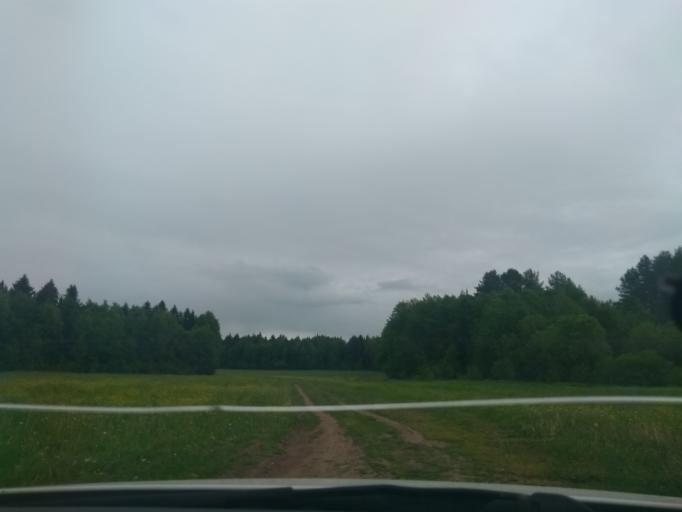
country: RU
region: Perm
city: Perm
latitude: 57.9846
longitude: 56.3307
